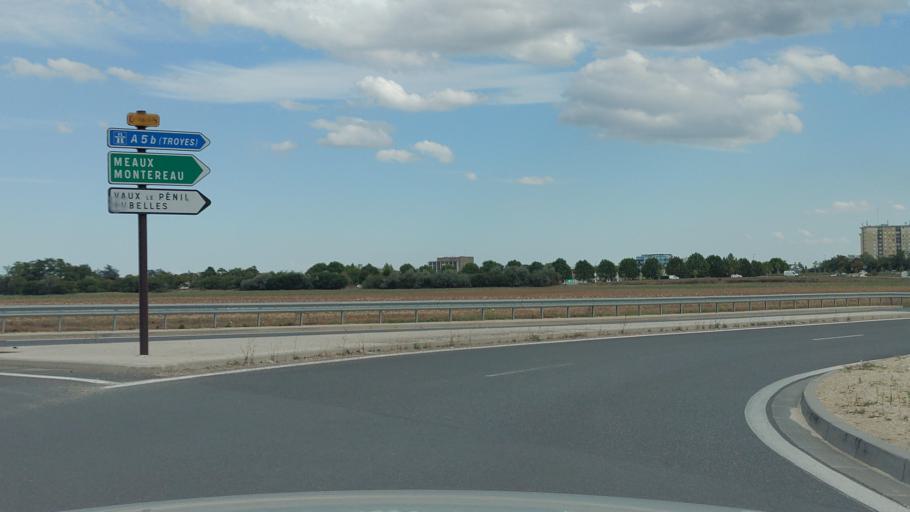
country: FR
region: Ile-de-France
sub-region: Departement de Seine-et-Marne
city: Rubelles
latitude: 48.5557
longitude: 2.6630
